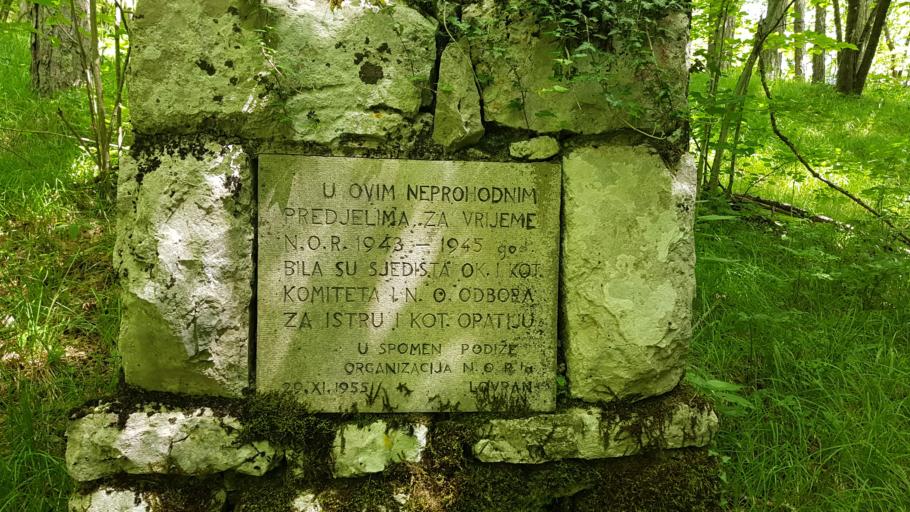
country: HR
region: Istarska
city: Lovran
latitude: 45.2943
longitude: 14.2374
